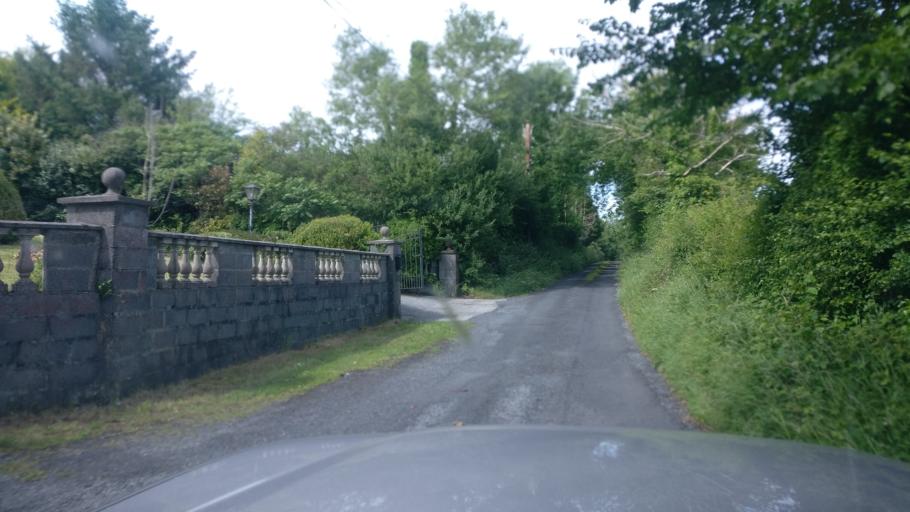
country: IE
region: Connaught
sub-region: County Galway
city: Gort
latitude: 53.0773
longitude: -8.7727
